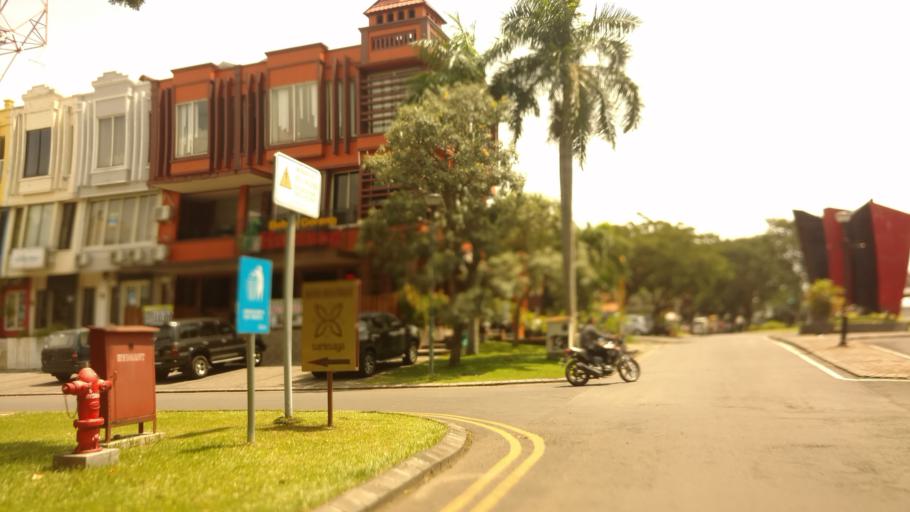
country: ID
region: East Java
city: Driyorejo
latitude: -7.2916
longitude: 112.6547
